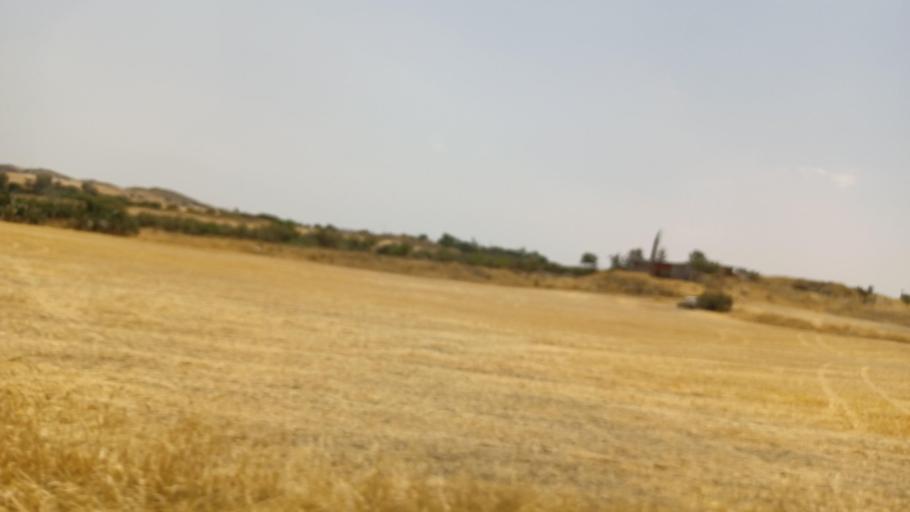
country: CY
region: Larnaka
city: Troulloi
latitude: 35.0187
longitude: 33.6072
